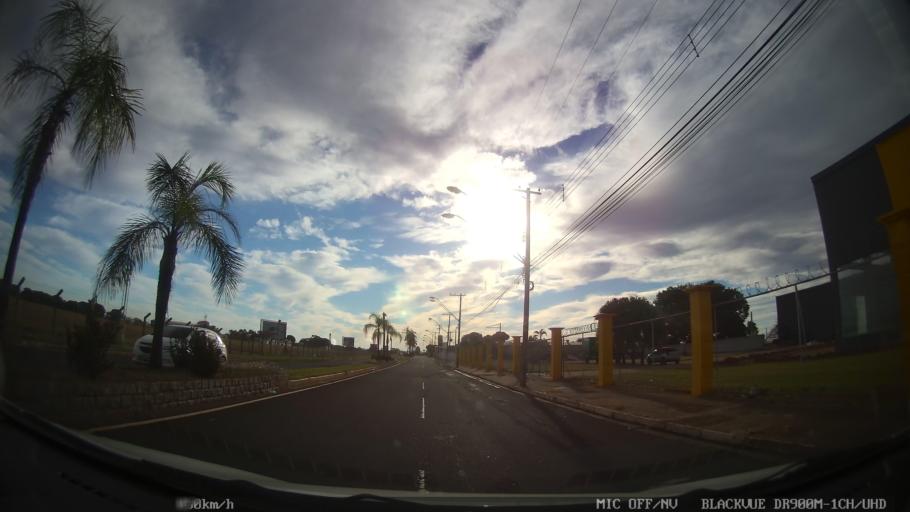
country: BR
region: Sao Paulo
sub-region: Catanduva
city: Catanduva
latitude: -21.1483
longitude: -48.9868
